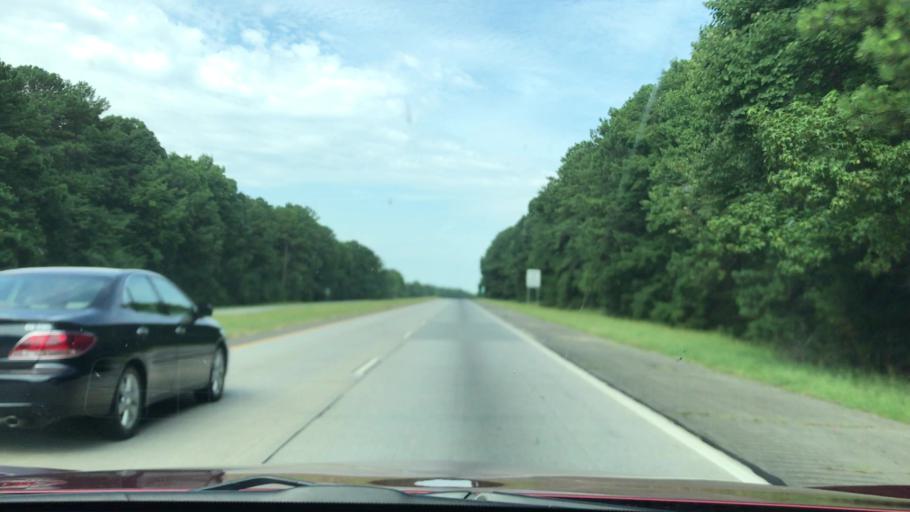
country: US
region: Georgia
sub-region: Warren County
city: Firing Range
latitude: 33.5029
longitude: -82.7728
